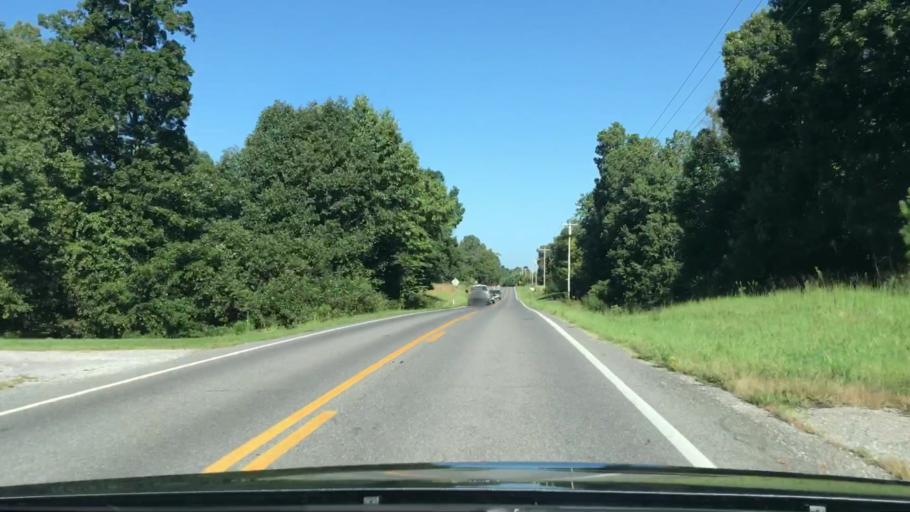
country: US
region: Kentucky
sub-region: Graves County
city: Mayfield
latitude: 36.7750
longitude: -88.5051
